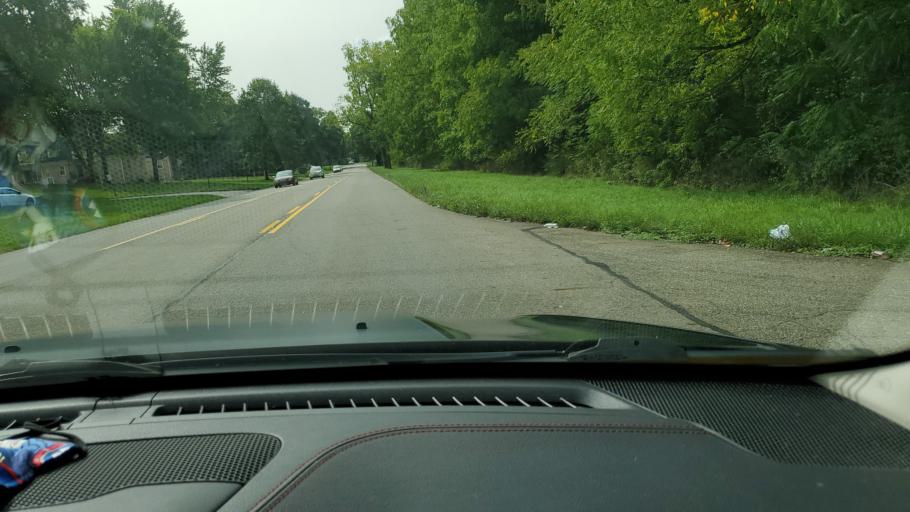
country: US
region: Ohio
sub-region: Mahoning County
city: Boardman
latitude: 41.0577
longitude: -80.6723
